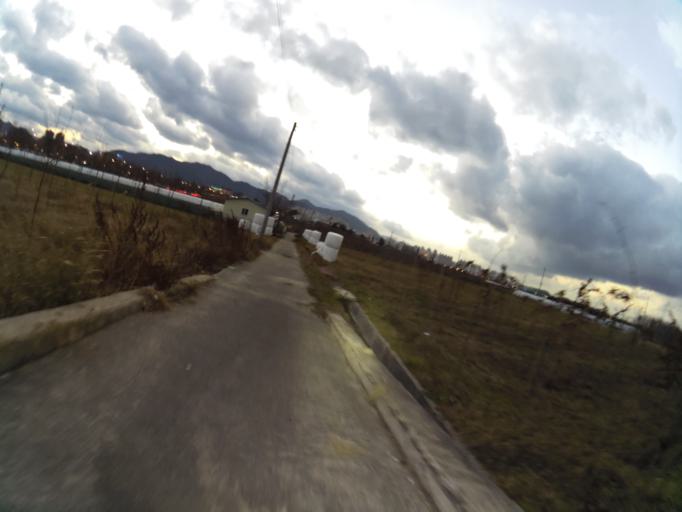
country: KR
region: Gyeongsangbuk-do
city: Gyeongsan-si
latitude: 35.8367
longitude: 128.7512
